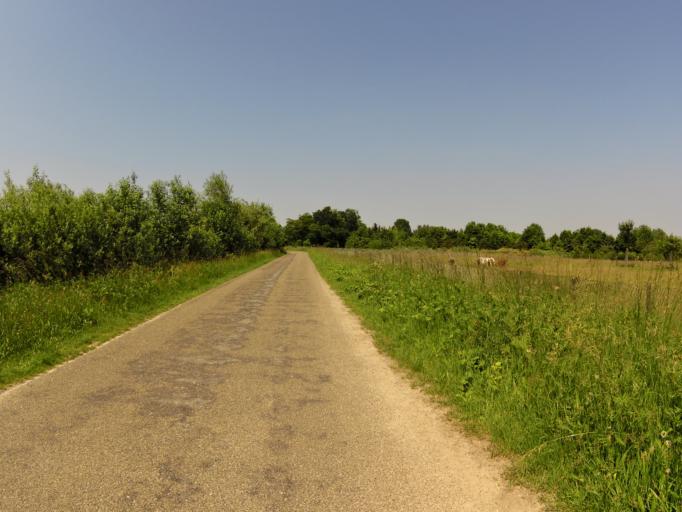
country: NL
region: North Brabant
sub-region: Gemeente Sint-Michielsgestel
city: Sint-Michielsgestel
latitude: 51.6214
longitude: 5.3481
